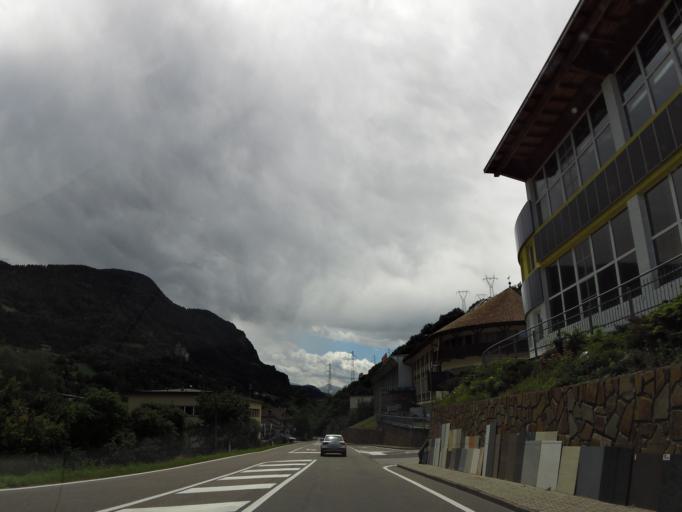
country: IT
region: Trentino-Alto Adige
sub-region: Bolzano
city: Ponte Gardena
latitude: 46.6064
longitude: 11.5332
